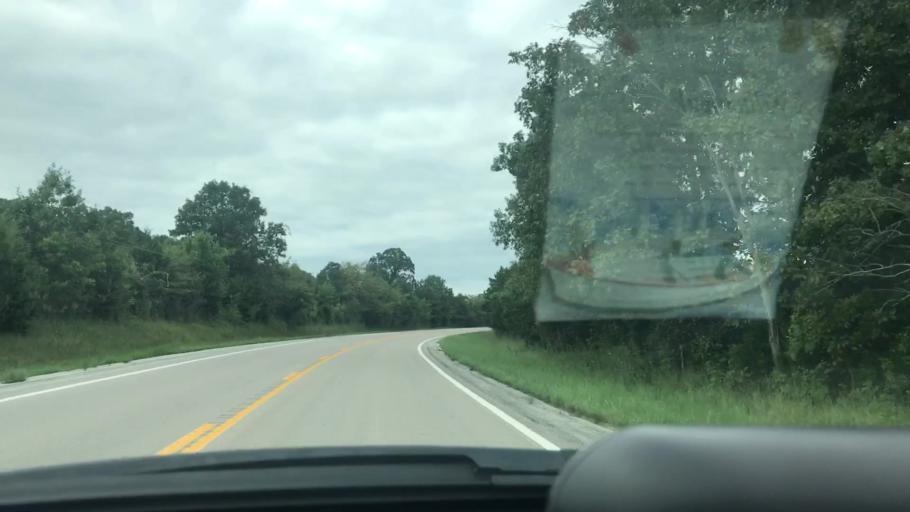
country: US
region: Missouri
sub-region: Benton County
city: Warsaw
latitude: 38.1247
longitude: -93.2798
